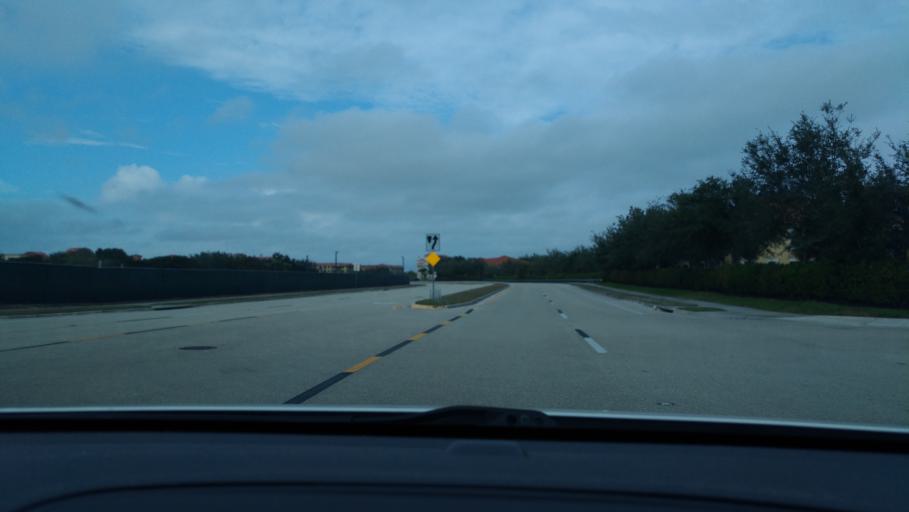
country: US
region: Florida
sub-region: Lee County
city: Estero
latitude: 26.3959
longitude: -81.8058
